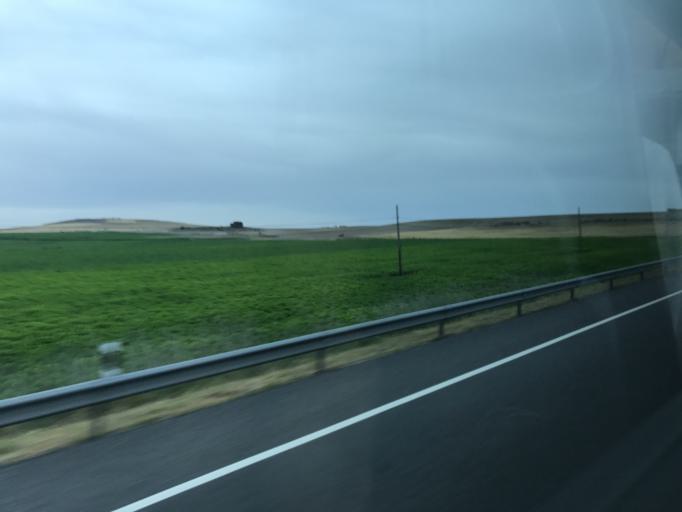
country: ES
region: Castille and Leon
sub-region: Provincia de Segovia
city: San Cristobal de la Vega
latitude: 41.1233
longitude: -4.6449
